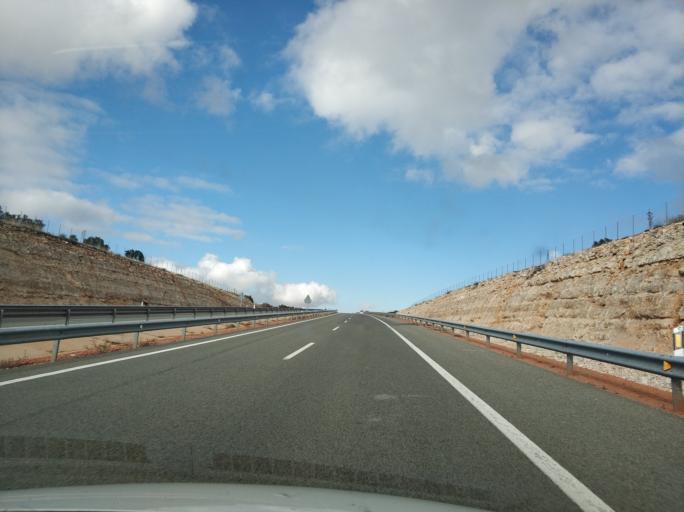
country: ES
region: Castille and Leon
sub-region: Provincia de Soria
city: Adradas
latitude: 41.2953
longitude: -2.4768
